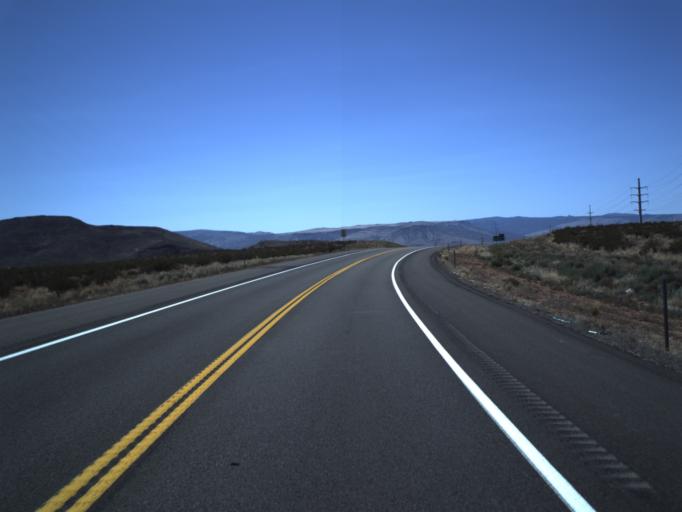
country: US
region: Utah
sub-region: Washington County
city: Washington
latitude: 37.0217
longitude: -113.4875
